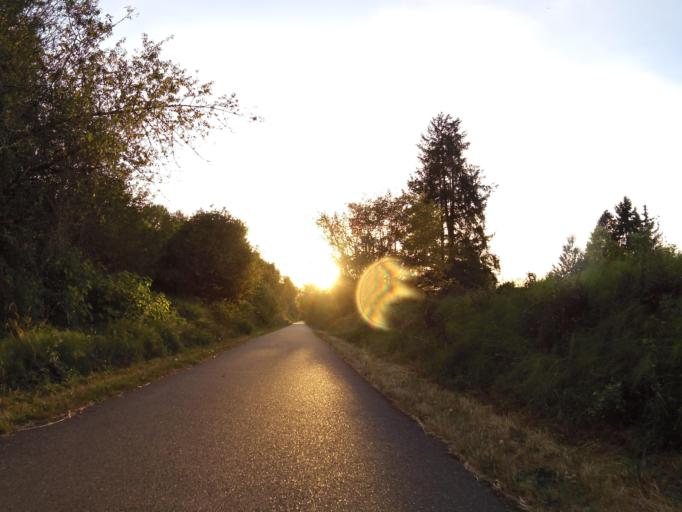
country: US
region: Washington
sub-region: Thurston County
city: Tenino
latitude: 46.8569
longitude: -122.8332
